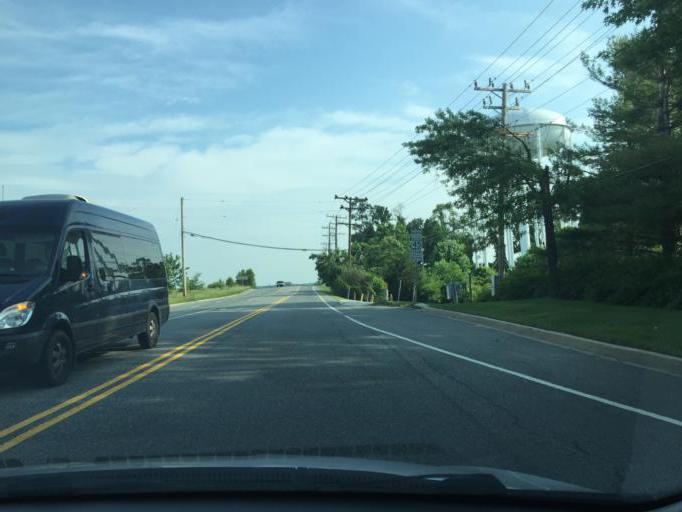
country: US
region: Maryland
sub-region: Baltimore County
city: Hunt Valley
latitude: 39.5205
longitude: -76.6432
